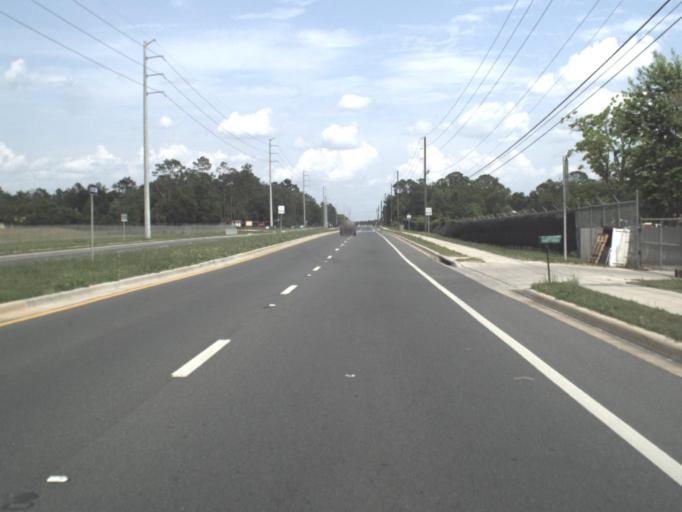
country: US
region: Florida
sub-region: Putnam County
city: Interlachen
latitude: 29.6285
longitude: -81.8102
